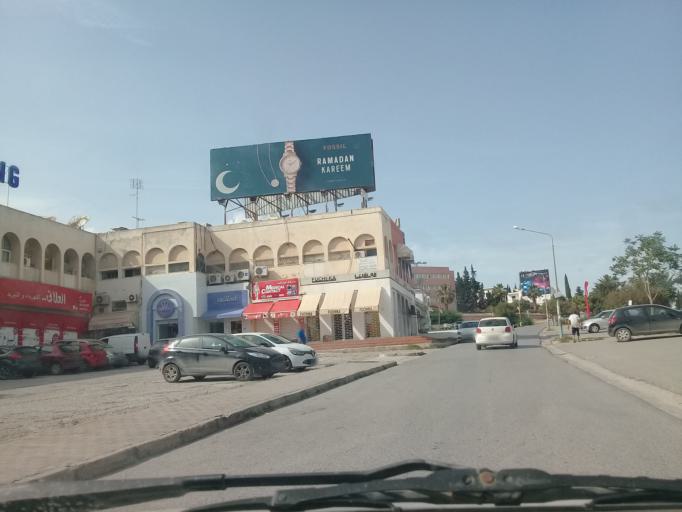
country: TN
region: Tunis
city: Tunis
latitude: 36.8466
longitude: 10.1672
